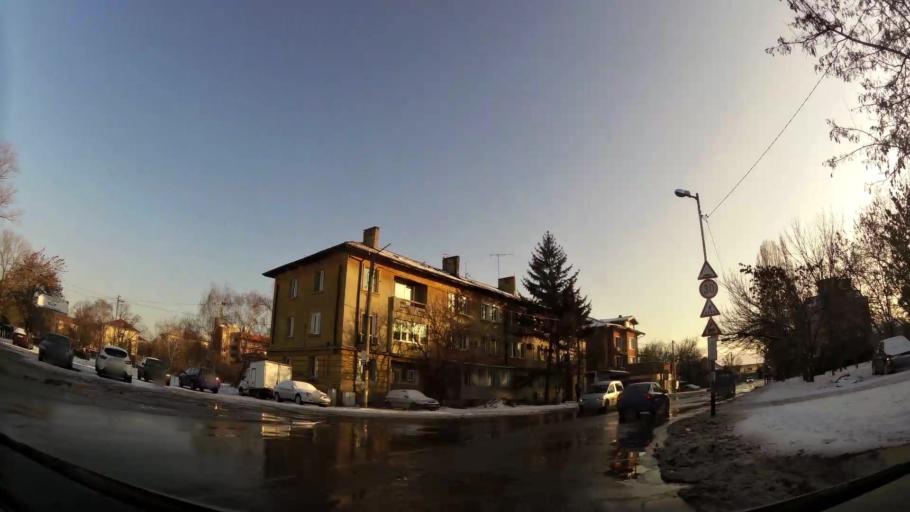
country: BG
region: Sofia-Capital
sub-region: Stolichna Obshtina
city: Sofia
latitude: 42.6796
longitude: 23.3787
